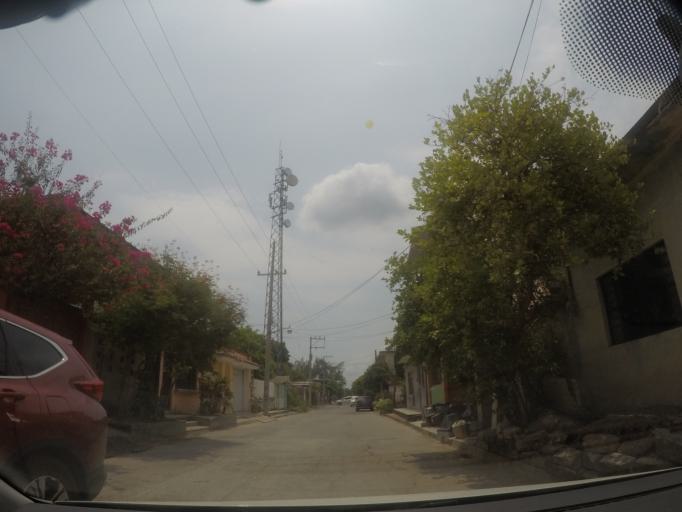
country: MX
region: Oaxaca
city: El Espinal
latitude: 16.4892
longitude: -95.0410
